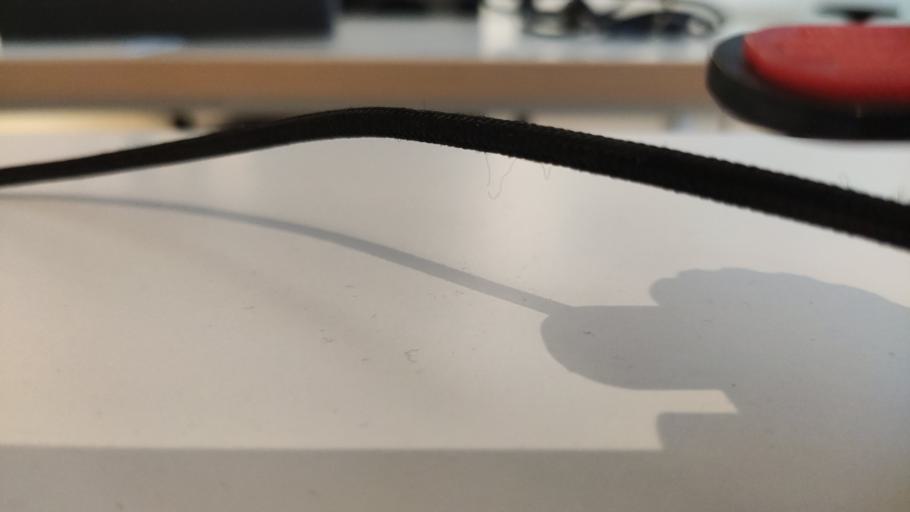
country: RU
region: Moskovskaya
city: Novopetrovskoye
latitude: 55.8582
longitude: 36.3801
